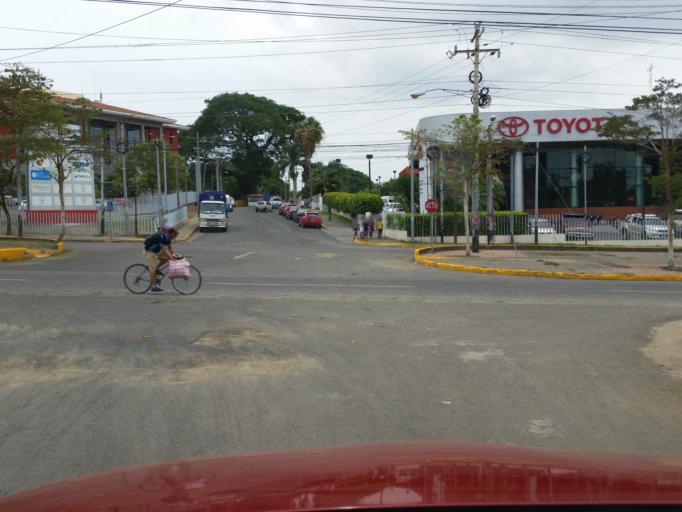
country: NI
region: Managua
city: Managua
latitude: 12.1296
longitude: -86.2805
